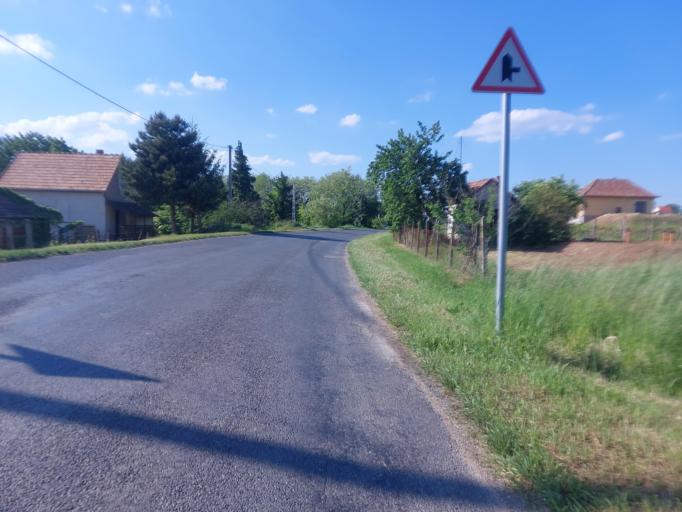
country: HU
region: Veszprem
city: Devecser
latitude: 47.1421
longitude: 17.3556
